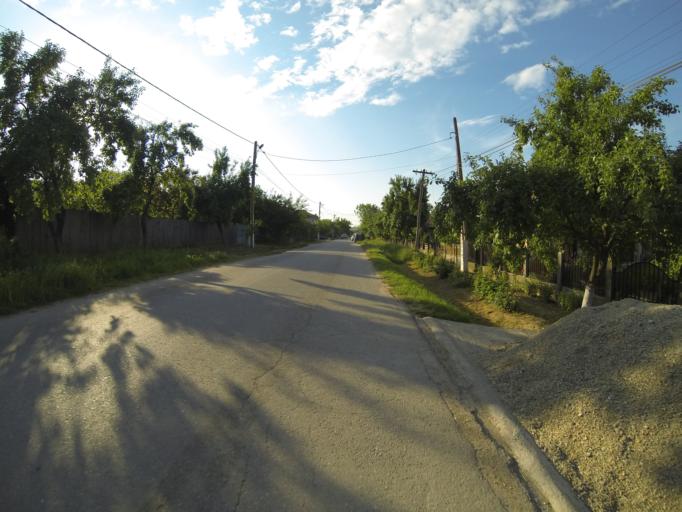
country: RO
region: Dolj
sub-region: Comuna Tuglui
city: Tuglui
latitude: 44.2037
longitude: 23.7985
